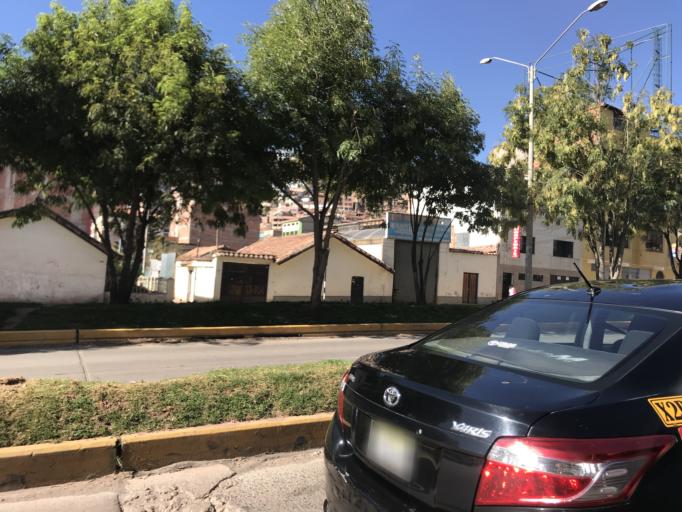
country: PE
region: Cusco
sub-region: Provincia de Cusco
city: Cusco
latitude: -13.5319
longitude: -71.9664
